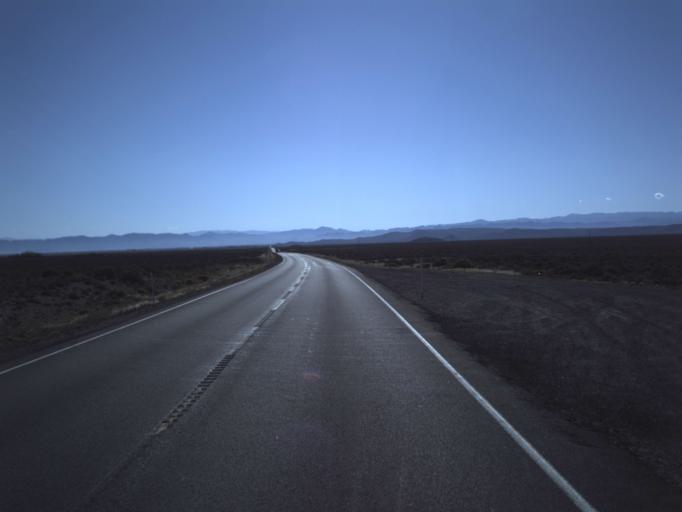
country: US
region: Utah
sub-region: Washington County
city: Enterprise
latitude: 37.7986
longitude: -113.9111
